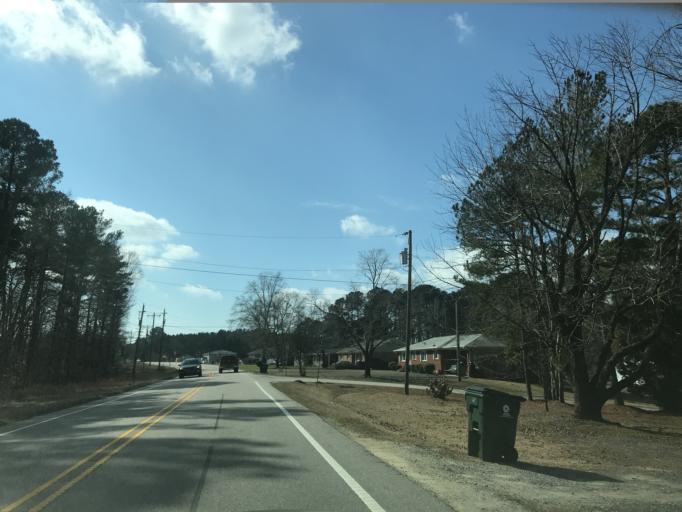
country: US
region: North Carolina
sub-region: Durham County
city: Gorman
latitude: 35.9683
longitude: -78.8037
